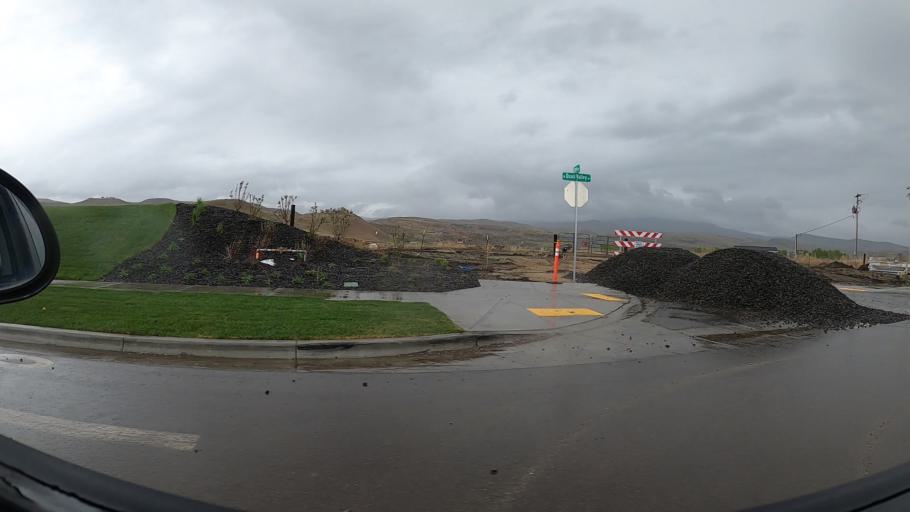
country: US
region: Idaho
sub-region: Ada County
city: Eagle
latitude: 43.7338
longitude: -116.2800
